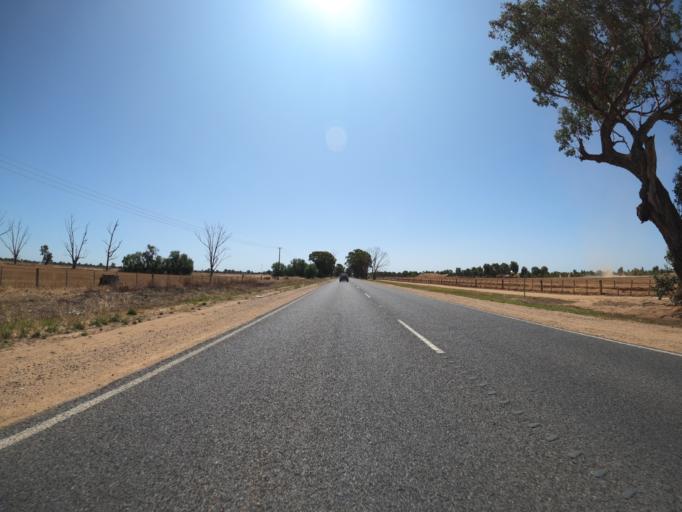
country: AU
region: Victoria
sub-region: Moira
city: Yarrawonga
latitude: -36.0156
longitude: 146.0446
